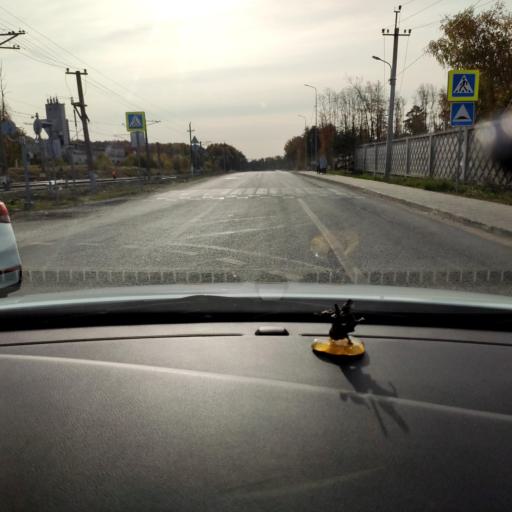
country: RU
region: Tatarstan
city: Vysokaya Gora
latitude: 55.9282
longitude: 49.2991
